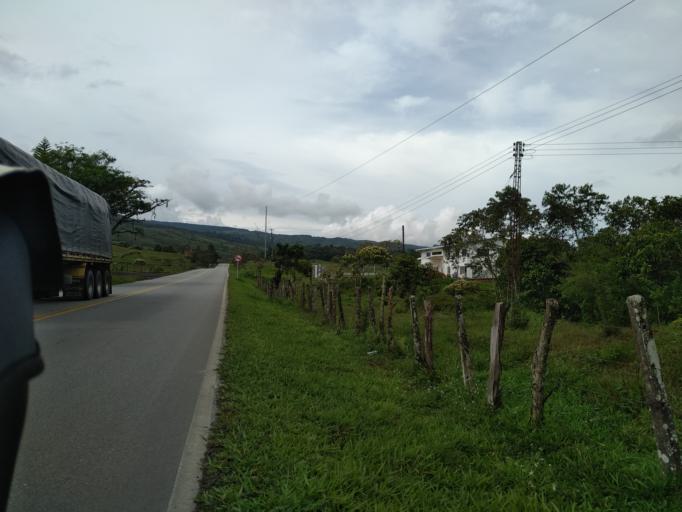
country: CO
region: Santander
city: Suaita
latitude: 6.1157
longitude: -73.3673
